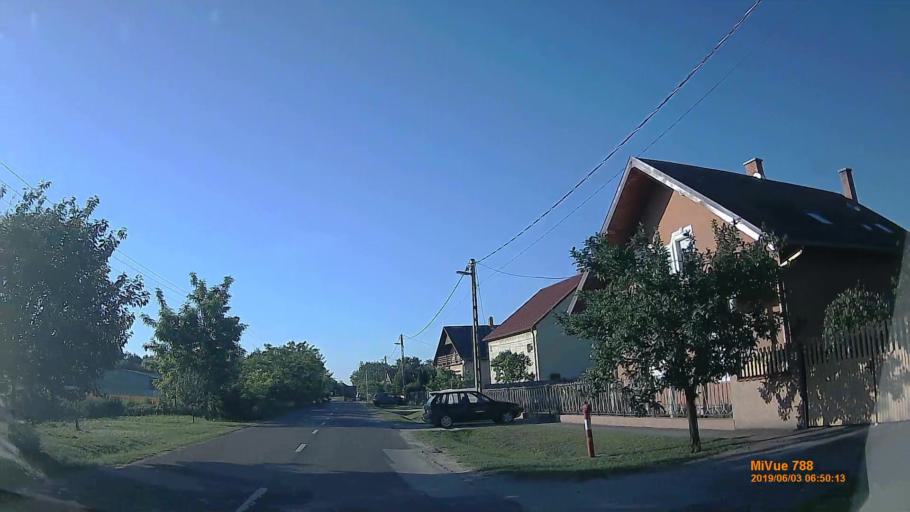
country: HU
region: Pest
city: Bugyi
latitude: 47.2213
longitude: 19.1705
